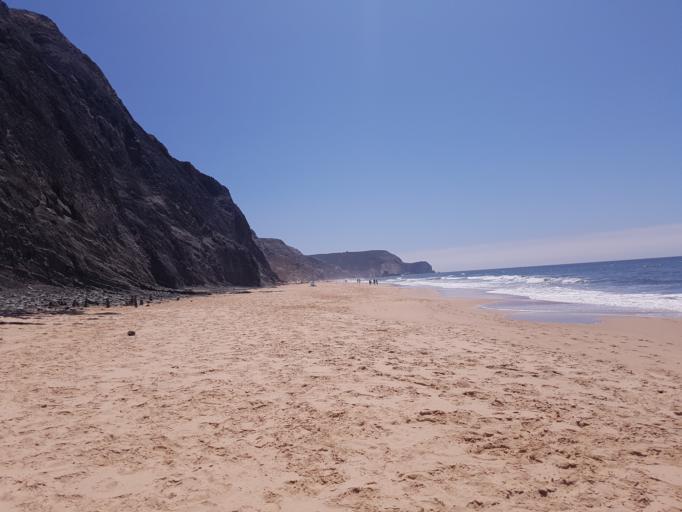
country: PT
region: Faro
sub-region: Vila do Bispo
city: Vila do Bispo
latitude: 37.1136
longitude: -8.9341
